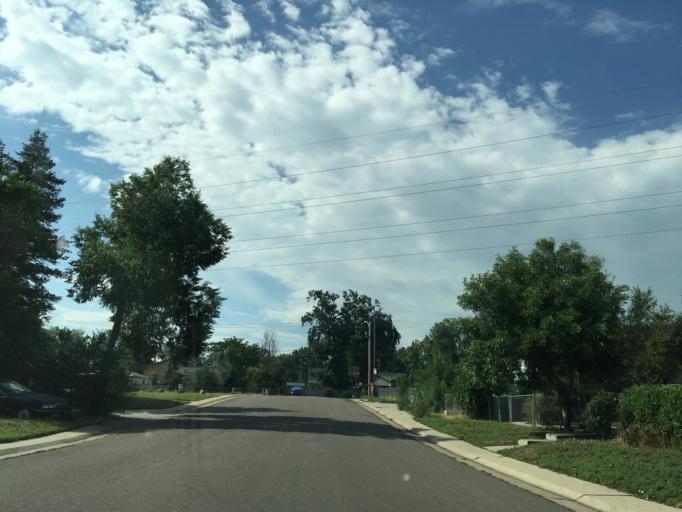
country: US
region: Colorado
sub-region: Jefferson County
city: Lakewood
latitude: 39.7011
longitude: -105.0409
